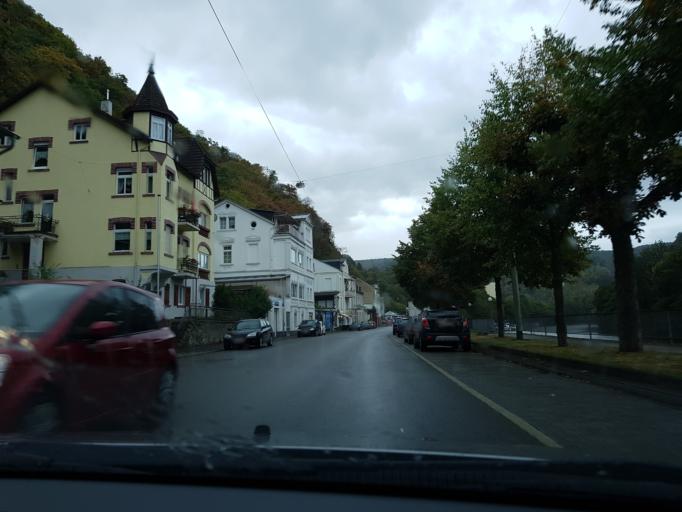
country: DE
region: Rheinland-Pfalz
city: Bad Ems
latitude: 50.3261
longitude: 7.7331
